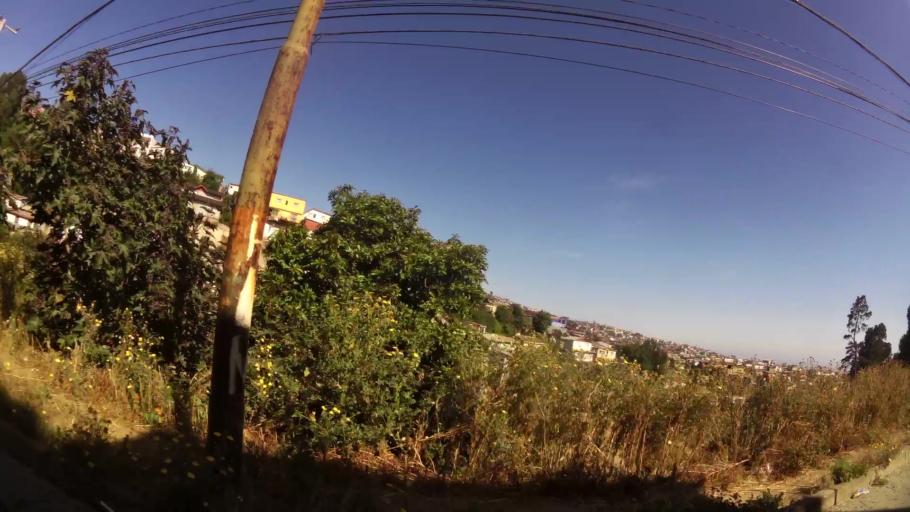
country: CL
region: Valparaiso
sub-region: Provincia de Valparaiso
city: Valparaiso
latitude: -33.0473
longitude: -71.6347
